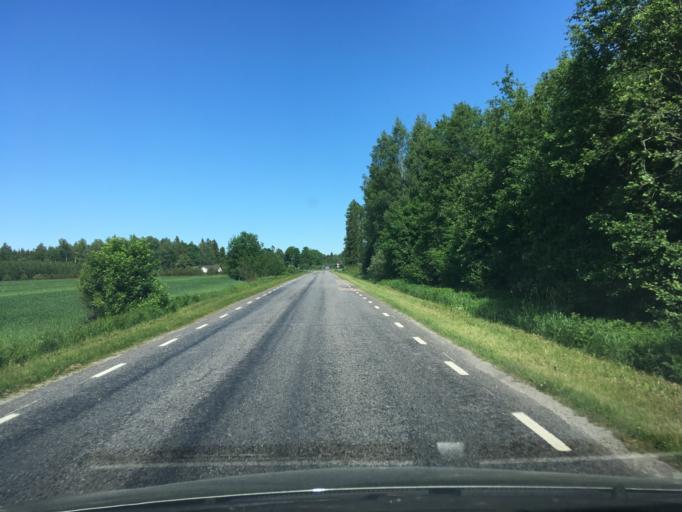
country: EE
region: Raplamaa
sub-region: Rapla vald
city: Rapla
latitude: 59.0653
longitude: 24.9130
